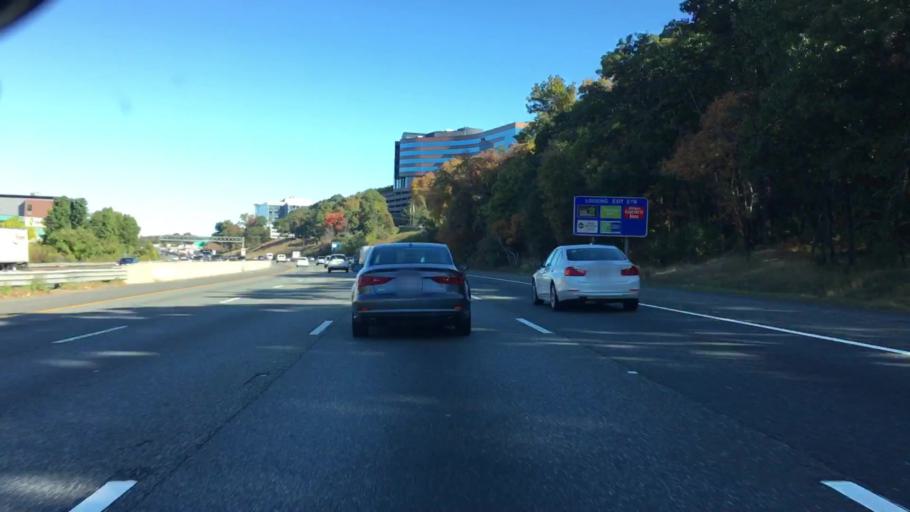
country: US
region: Massachusetts
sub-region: Middlesex County
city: Waltham
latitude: 42.3860
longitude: -71.2621
